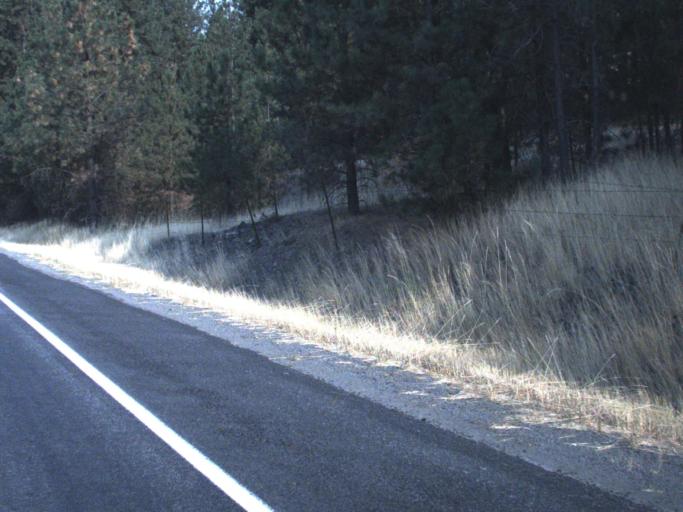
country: US
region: Idaho
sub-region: Benewah County
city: Plummer
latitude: 47.4389
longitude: -117.0987
